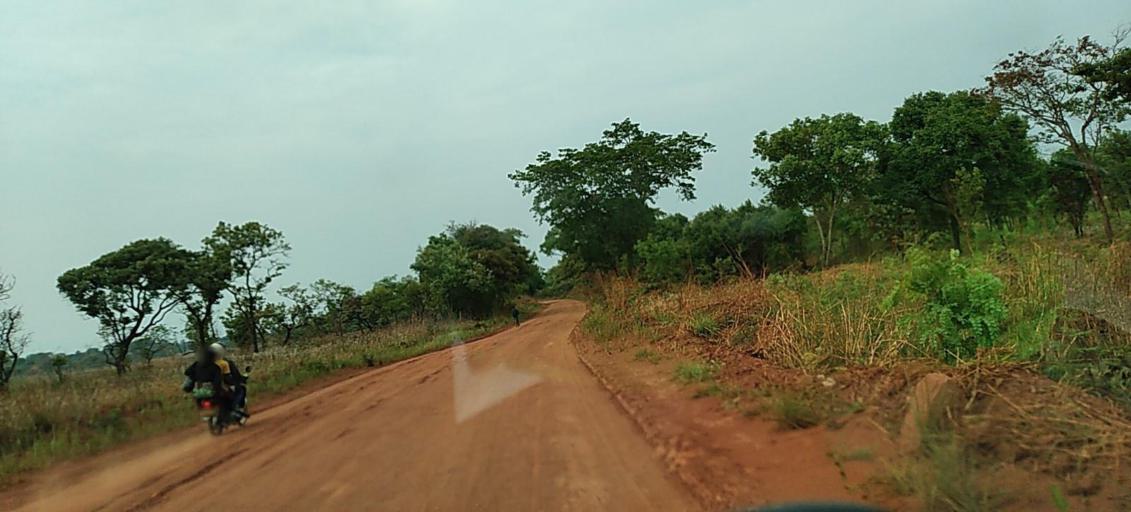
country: ZM
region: North-Western
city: Solwezi
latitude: -12.2244
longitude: 26.5108
